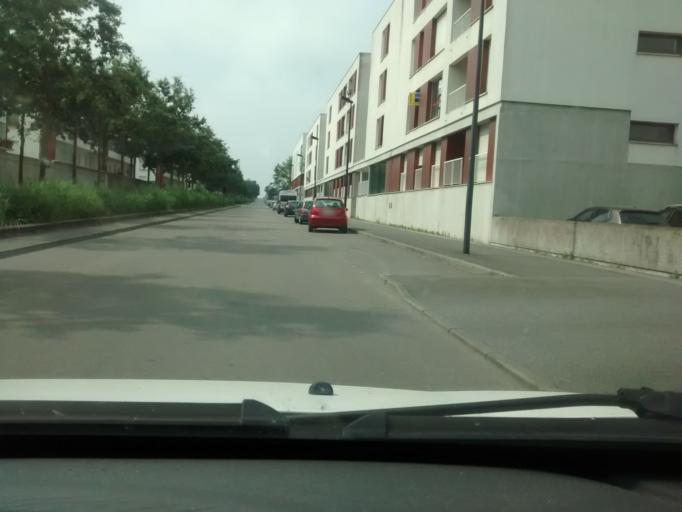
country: FR
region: Brittany
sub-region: Departement d'Ille-et-Vilaine
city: Saint-Jacques-de-la-Lande
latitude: 48.0824
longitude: -1.7154
